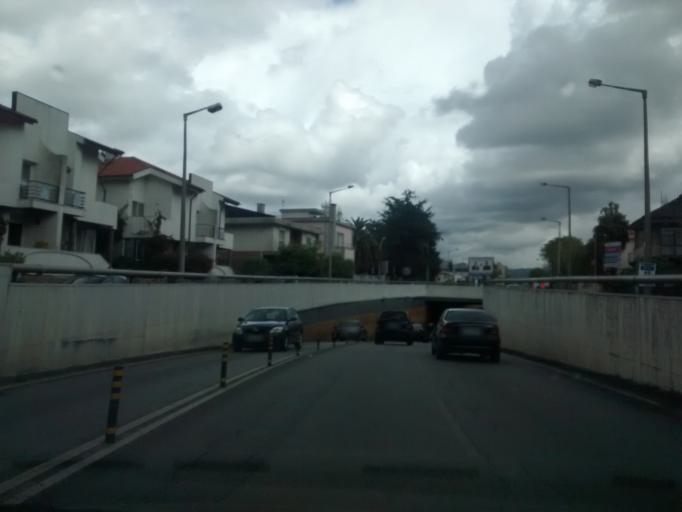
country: PT
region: Braga
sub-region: Braga
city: Braga
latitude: 41.5485
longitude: -8.4164
